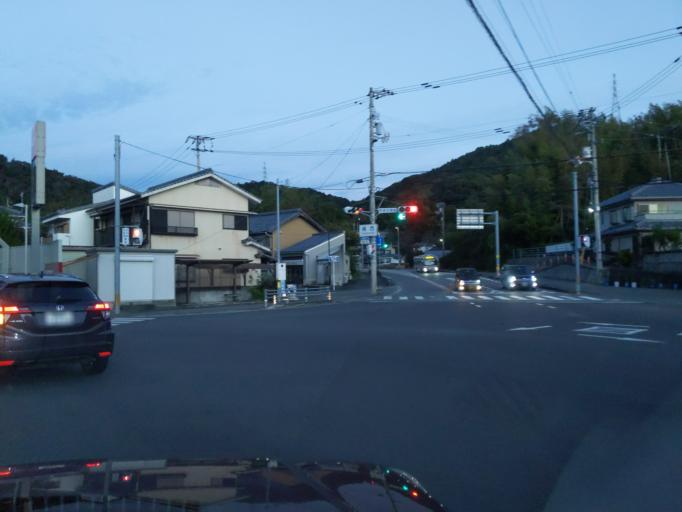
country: JP
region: Tokushima
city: Anan
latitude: 33.8731
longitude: 134.6375
